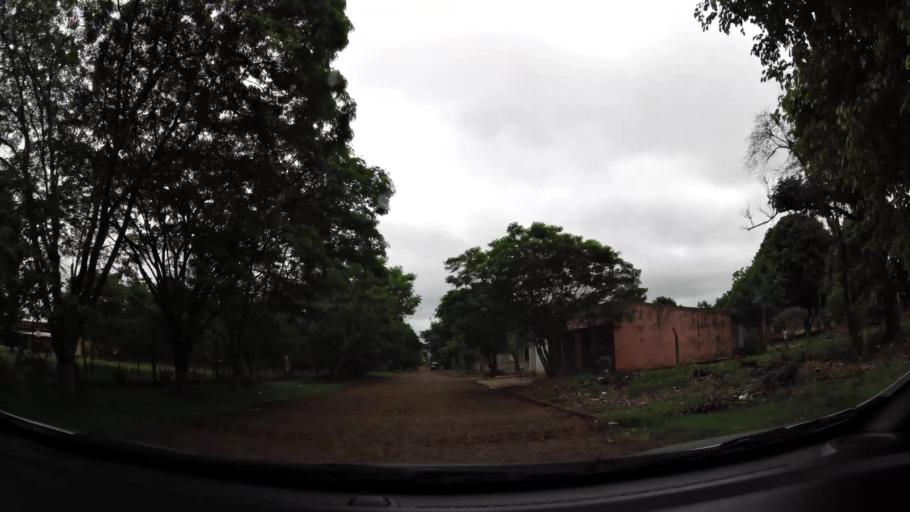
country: PY
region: Alto Parana
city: Presidente Franco
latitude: -25.4845
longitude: -54.7928
